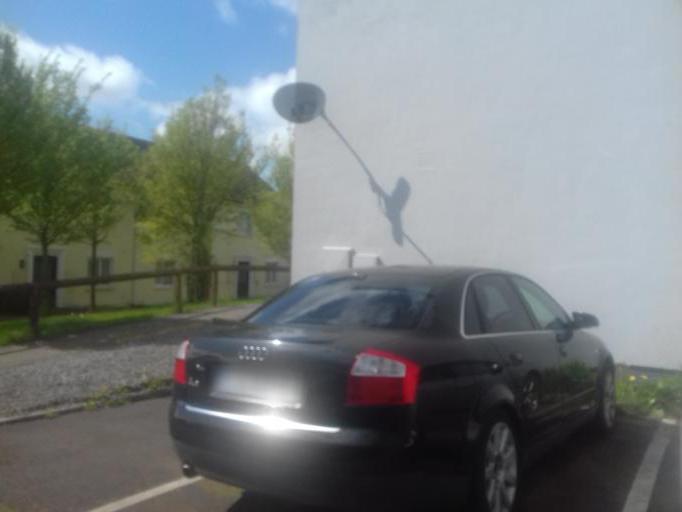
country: IE
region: Leinster
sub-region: Laois
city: Portlaoise
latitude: 53.0424
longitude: -7.2938
